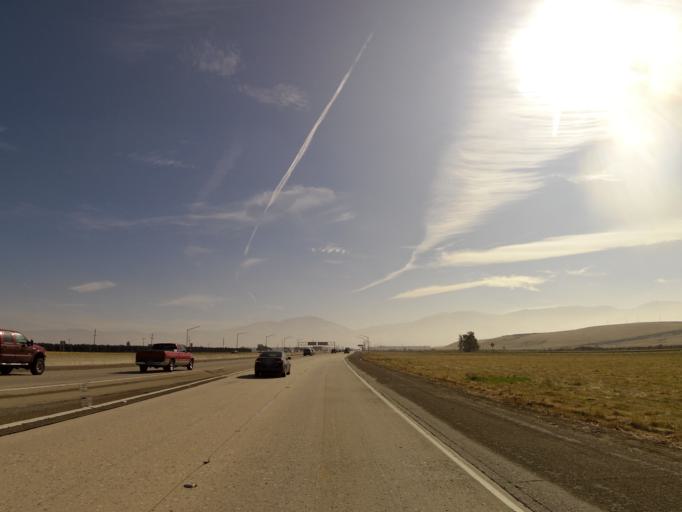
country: US
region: California
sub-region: Kern County
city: Frazier Park
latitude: 35.0107
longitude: -118.9535
